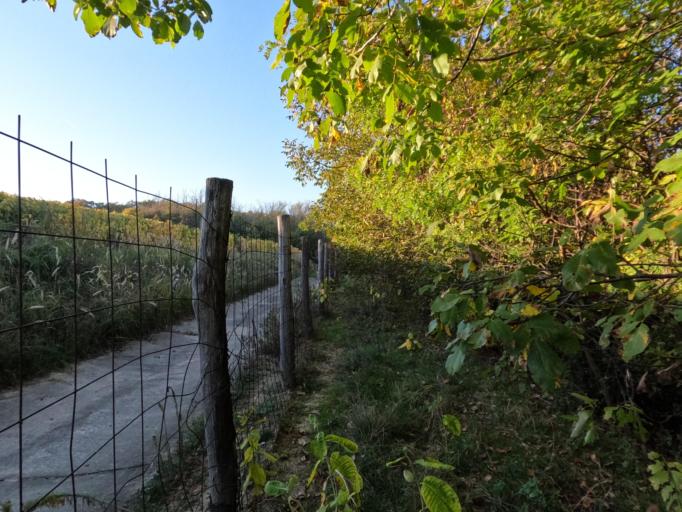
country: HU
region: Tolna
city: Szekszard
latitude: 46.3113
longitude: 18.6565
